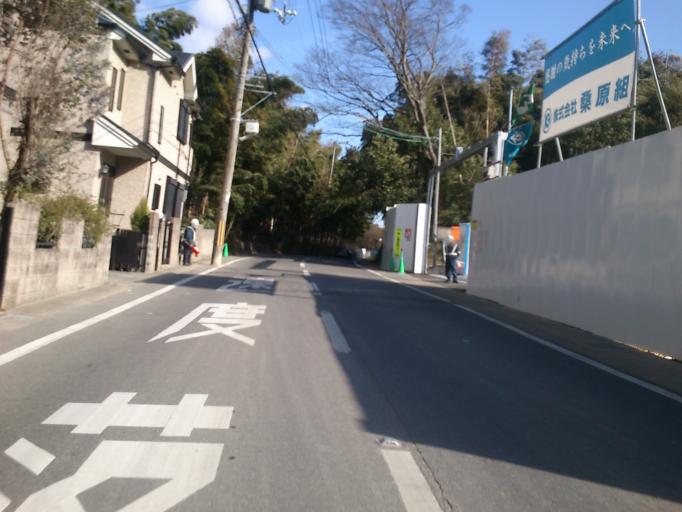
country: JP
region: Kyoto
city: Yawata
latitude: 34.9138
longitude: 135.6771
